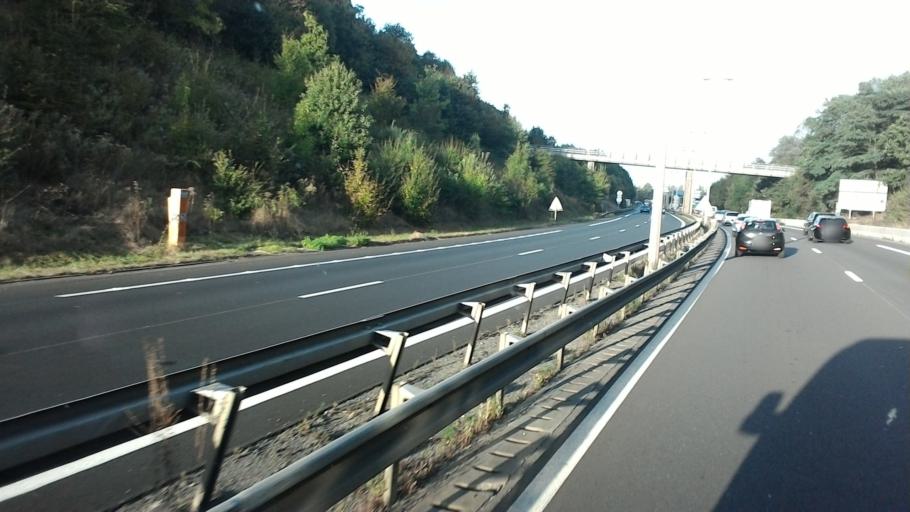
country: FR
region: Lorraine
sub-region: Departement de la Moselle
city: Terville
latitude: 49.3462
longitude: 6.1207
